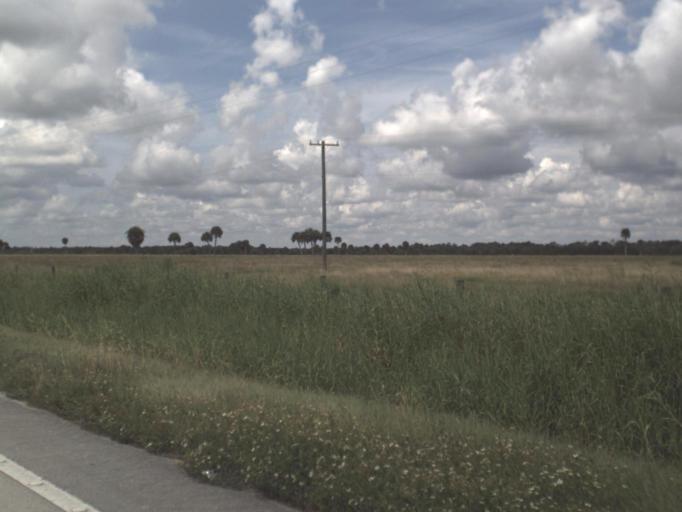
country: US
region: Florida
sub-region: Okeechobee County
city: Okeechobee
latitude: 27.2436
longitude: -80.9463
